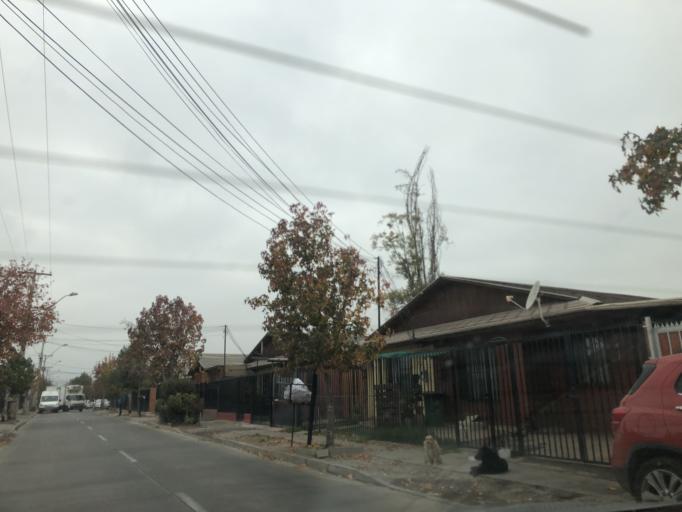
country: CL
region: Santiago Metropolitan
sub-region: Provincia de Santiago
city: La Pintana
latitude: -33.5797
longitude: -70.6091
